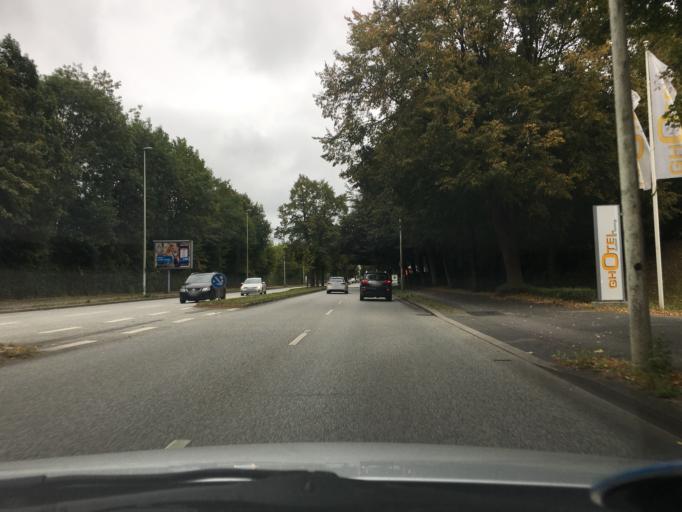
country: DE
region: Schleswig-Holstein
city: Kronshagen
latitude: 54.3384
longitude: 10.1053
